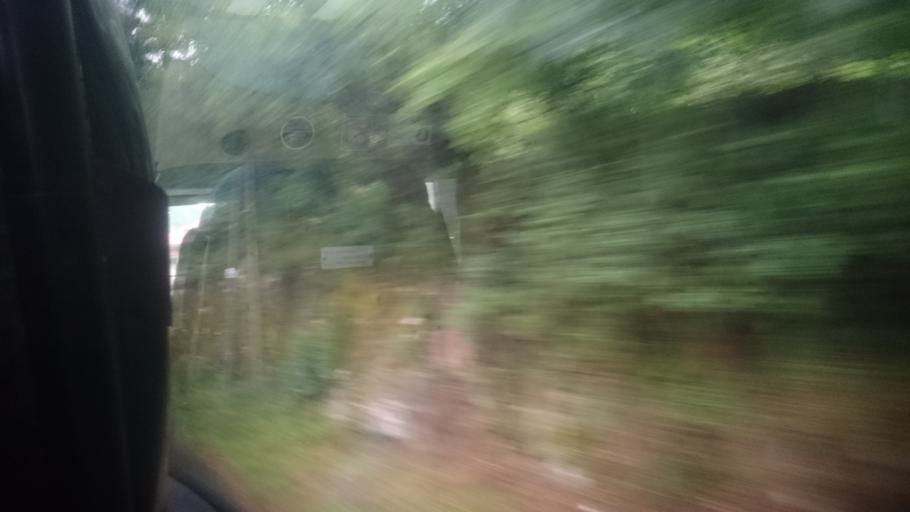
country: ES
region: Asturias
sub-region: Province of Asturias
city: Cangas de Onis
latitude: 43.3267
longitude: -5.0792
